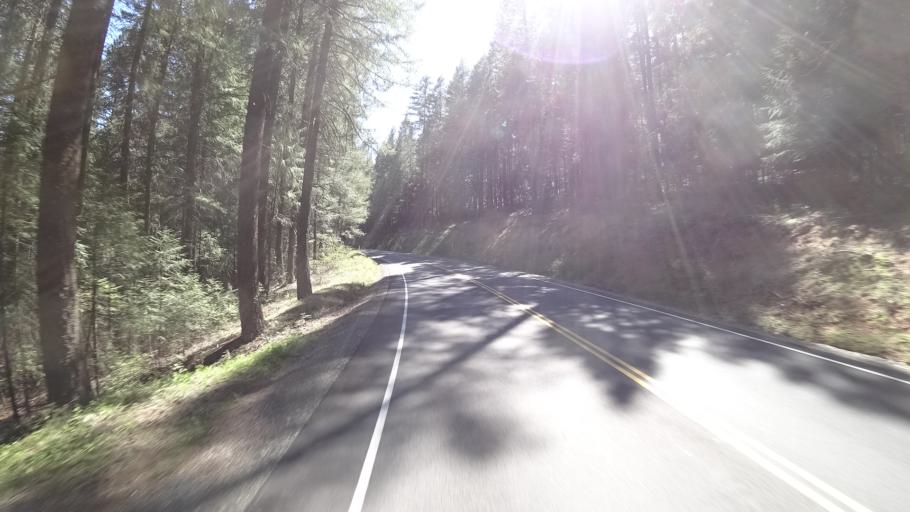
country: US
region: California
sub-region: Trinity County
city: Lewiston
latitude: 40.9133
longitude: -122.7738
